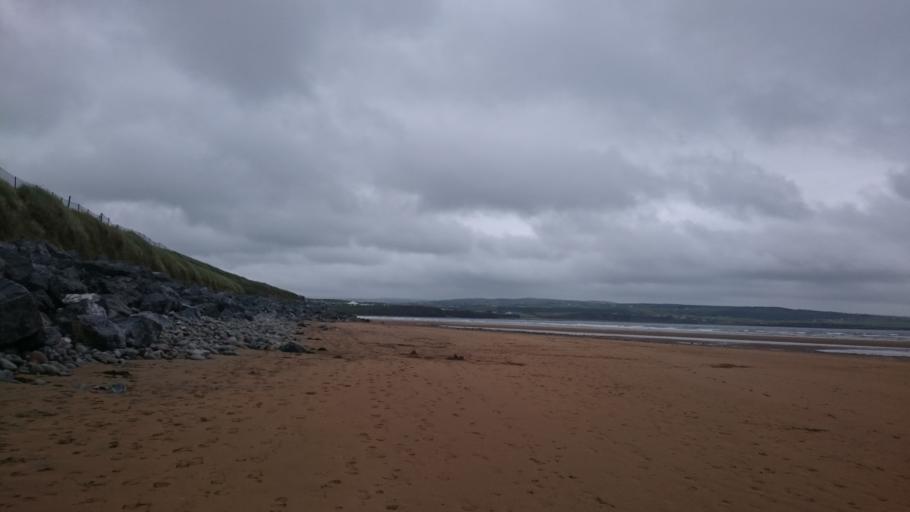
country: IE
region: Munster
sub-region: An Clar
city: Kilrush
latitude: 52.9412
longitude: -9.3584
